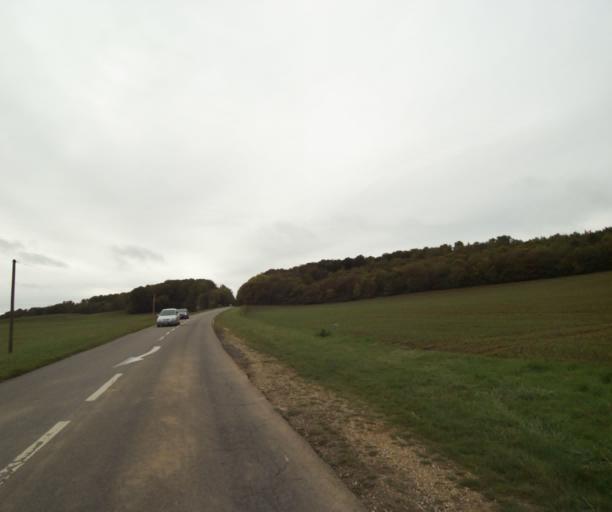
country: FR
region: Centre
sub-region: Departement d'Eure-et-Loir
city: Dreux
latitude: 48.7715
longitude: 1.3705
